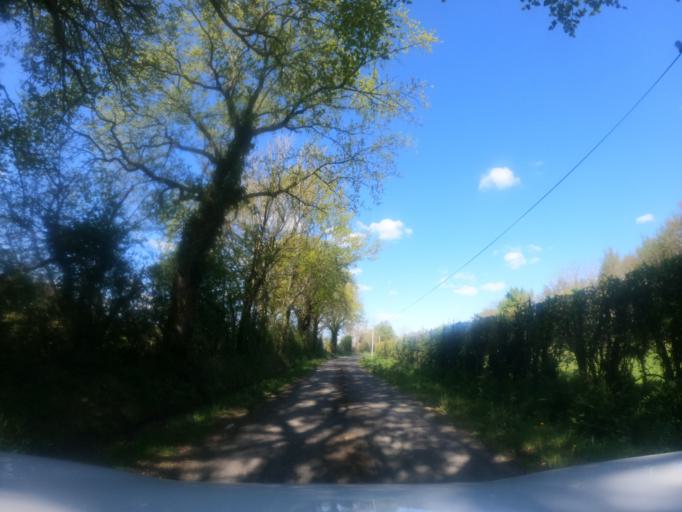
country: FR
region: Pays de la Loire
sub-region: Departement de la Vendee
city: Saint-Vincent-sur-Graon
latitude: 46.5276
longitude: -1.3647
